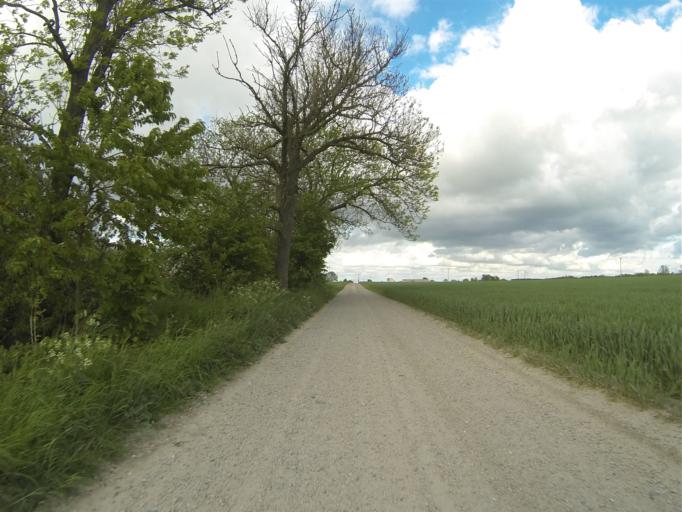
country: SE
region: Skane
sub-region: Lunds Kommun
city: Lund
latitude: 55.6998
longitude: 13.3078
